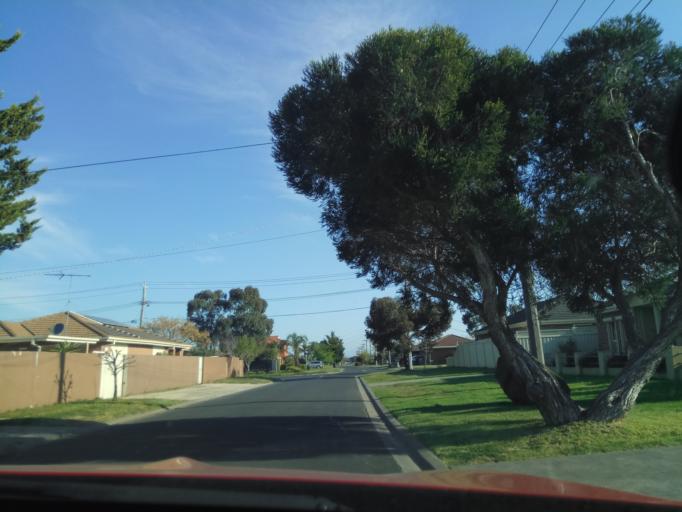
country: AU
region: Victoria
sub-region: Hobsons Bay
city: Laverton
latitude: -37.8732
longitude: 144.7717
